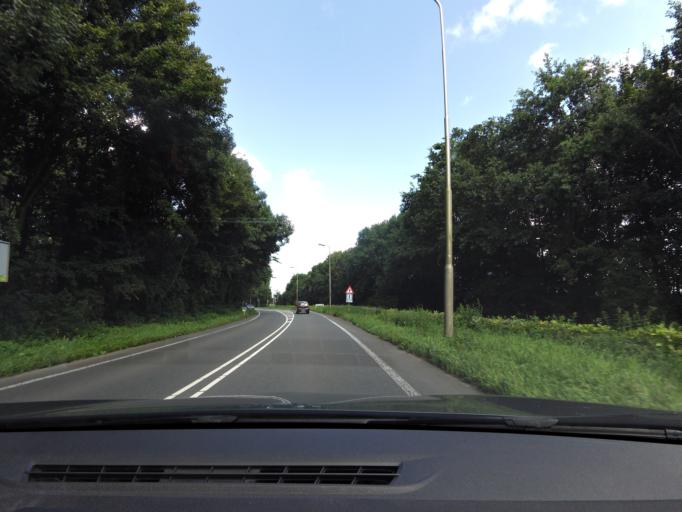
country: NL
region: South Holland
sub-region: Gemeente Alphen aan den Rijn
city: Alphen aan den Rijn
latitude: 52.1435
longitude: 4.7060
